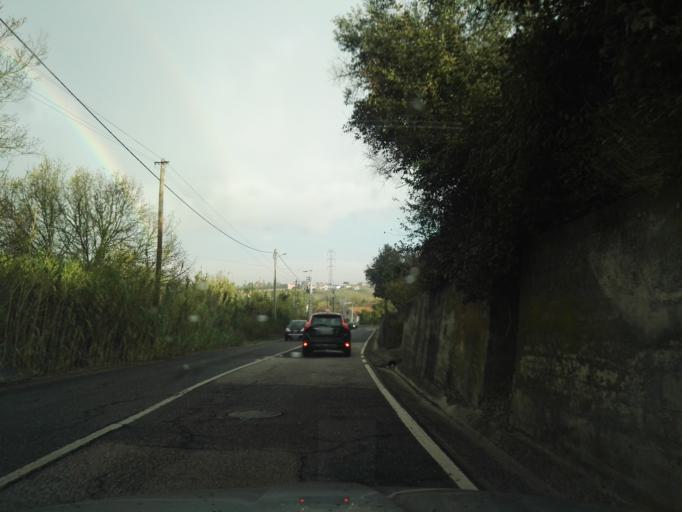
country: PT
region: Lisbon
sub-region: Arruda Dos Vinhos
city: Arruda dos Vinhos
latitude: 38.9696
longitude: -9.0650
